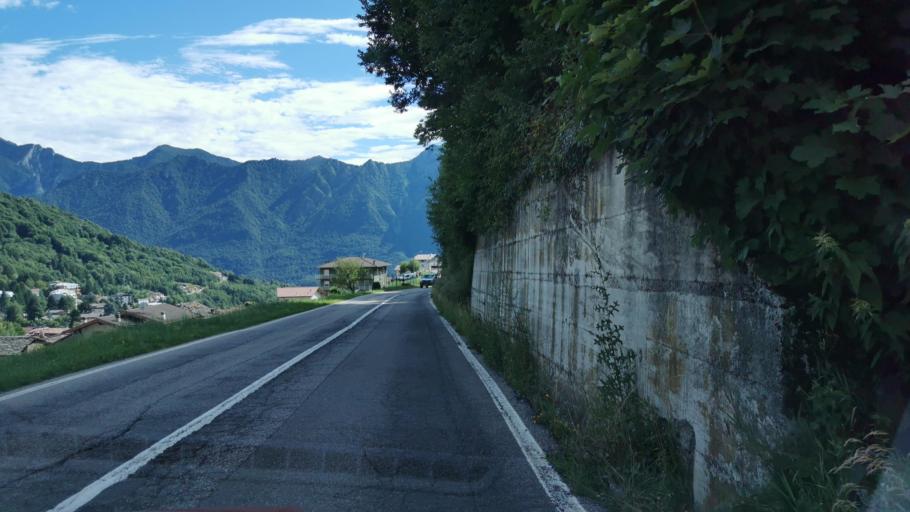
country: IT
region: Lombardy
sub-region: Provincia di Lecco
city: Casargo
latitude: 46.0377
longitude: 9.3848
